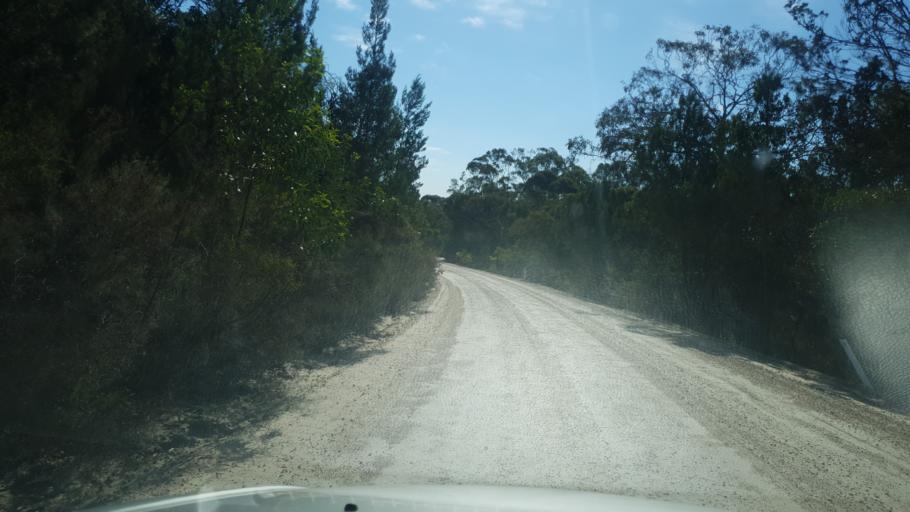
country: AU
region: South Australia
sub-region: Barossa
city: Williamstown
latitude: -34.6506
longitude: 138.8324
